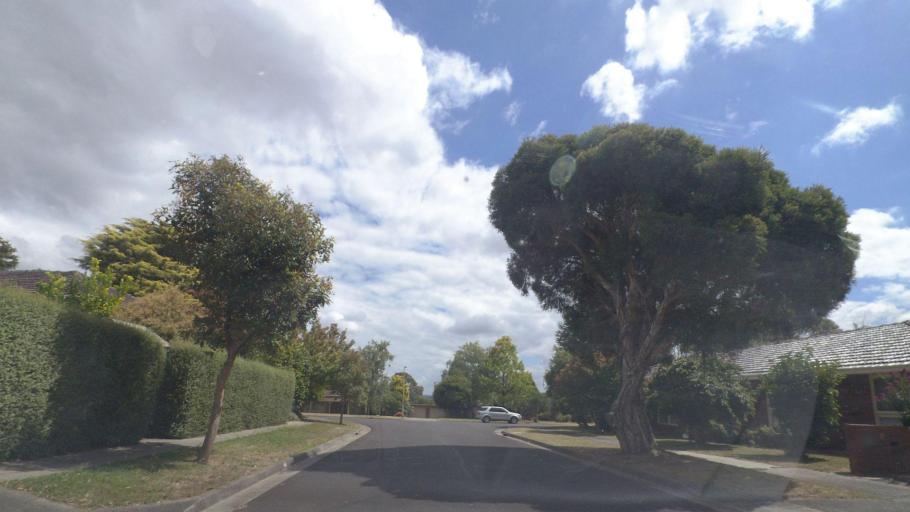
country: AU
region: Victoria
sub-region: Knox
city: Boronia
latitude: -37.8640
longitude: 145.2900
